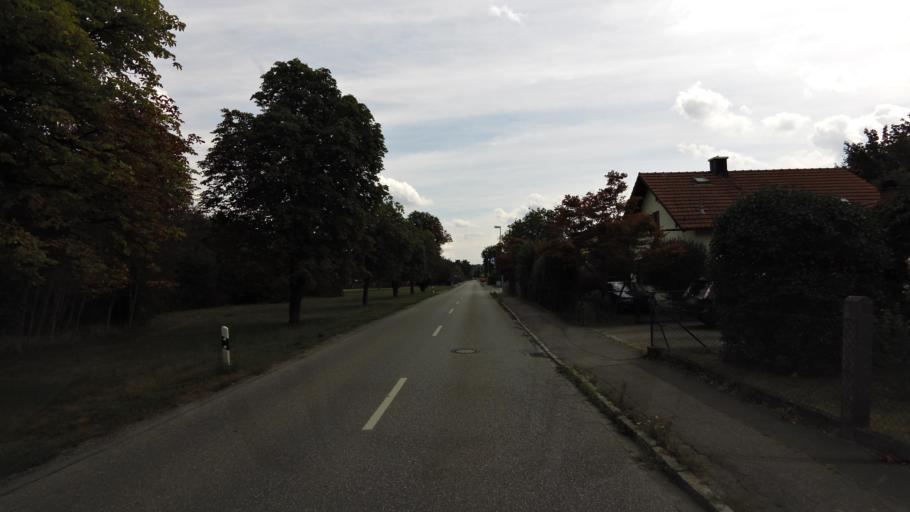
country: DE
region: Bavaria
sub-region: Upper Bavaria
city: Unterneukirchen
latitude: 48.1499
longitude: 12.6159
